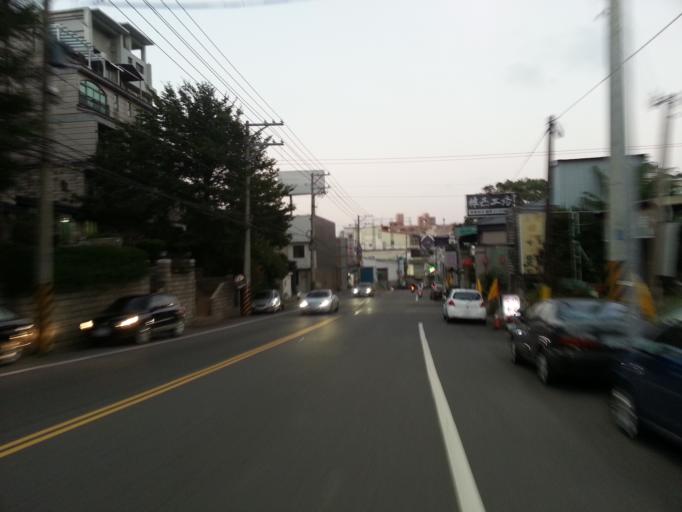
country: TW
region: Taiwan
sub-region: Hsinchu
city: Hsinchu
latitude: 24.7814
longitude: 120.9669
